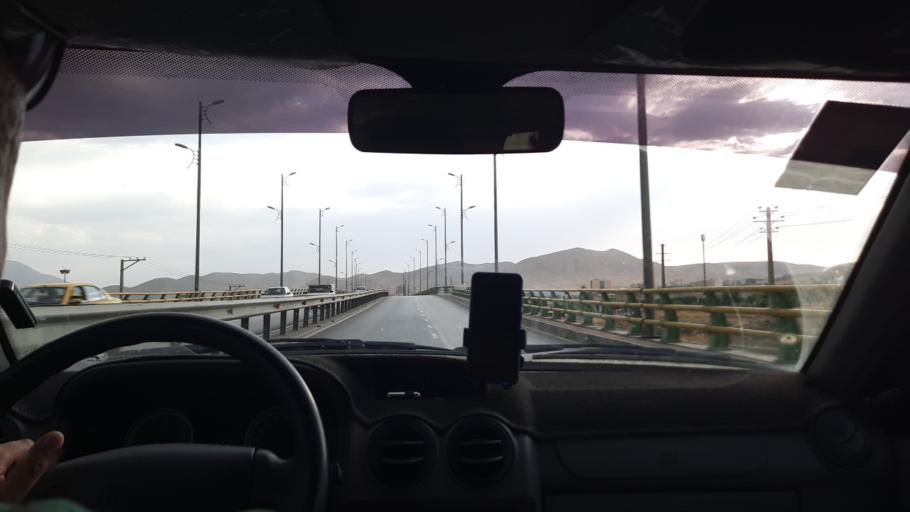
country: IR
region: Markazi
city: Arak
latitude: 34.0781
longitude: 49.6481
